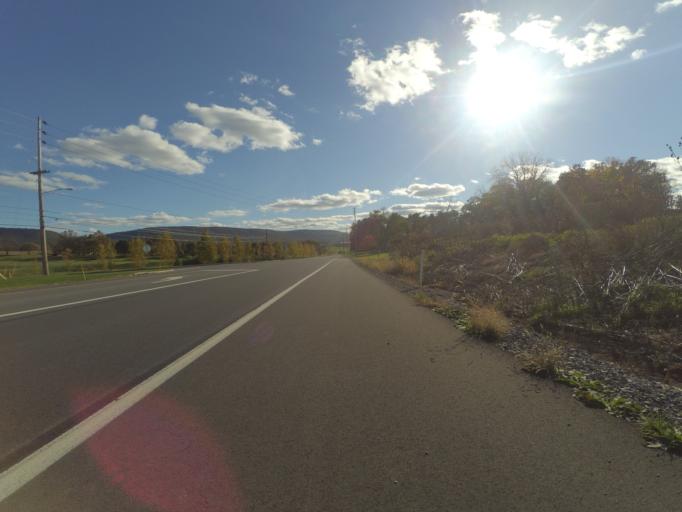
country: US
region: Pennsylvania
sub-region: Centre County
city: Pleasant Gap
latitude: 40.8675
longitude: -77.7804
